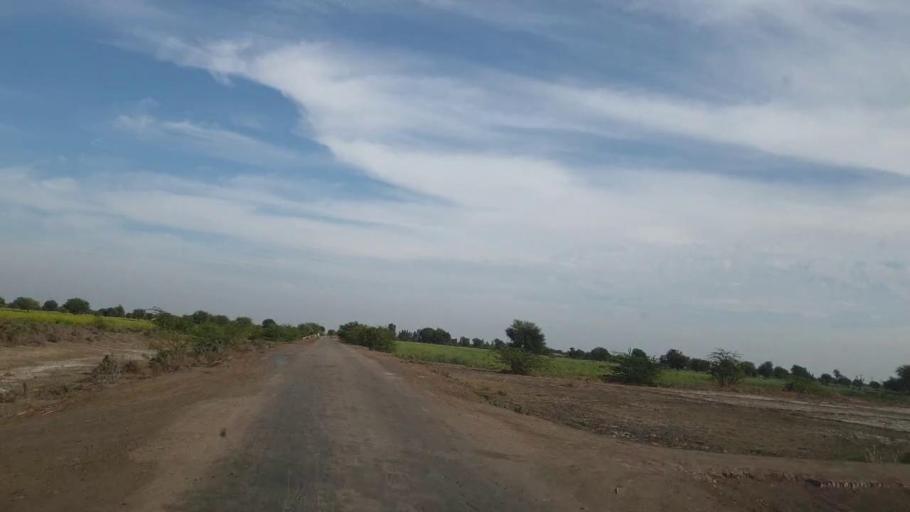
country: PK
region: Sindh
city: Pithoro
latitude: 25.6338
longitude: 69.3973
